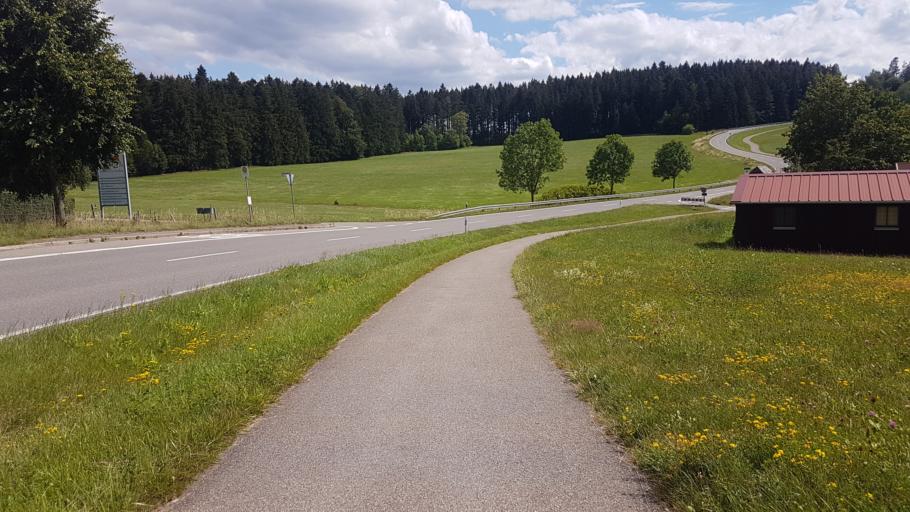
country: DE
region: Baden-Wuerttemberg
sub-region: Freiburg Region
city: Hardt
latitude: 48.1952
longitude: 8.4135
